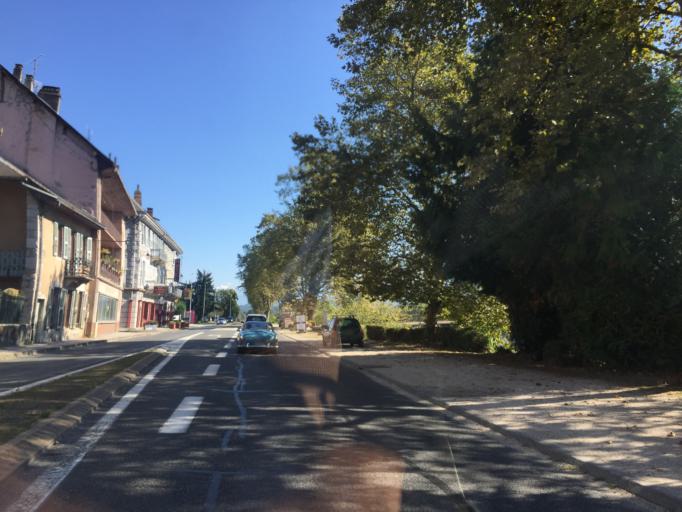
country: FR
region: Rhone-Alpes
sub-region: Departement de la Savoie
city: Montmelian
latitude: 45.4986
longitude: 6.0589
